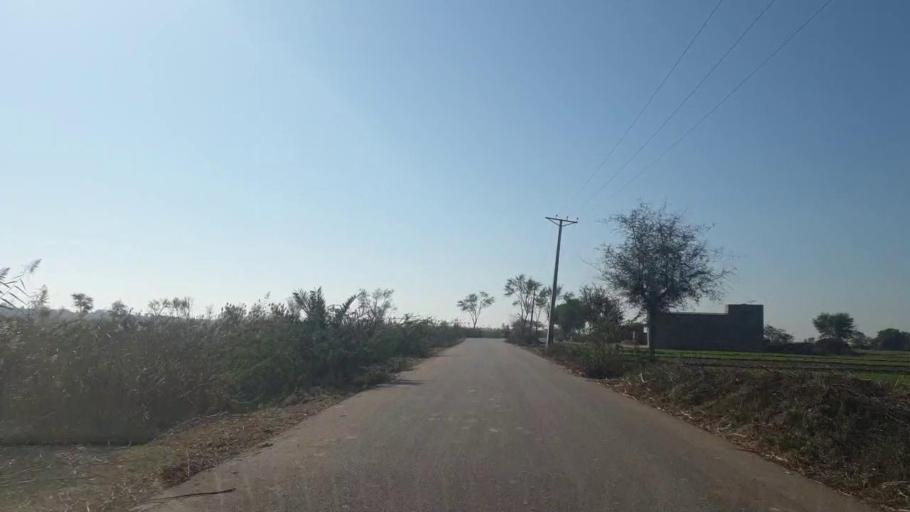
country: PK
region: Sindh
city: Kot Diji
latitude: 27.3110
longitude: 68.6478
